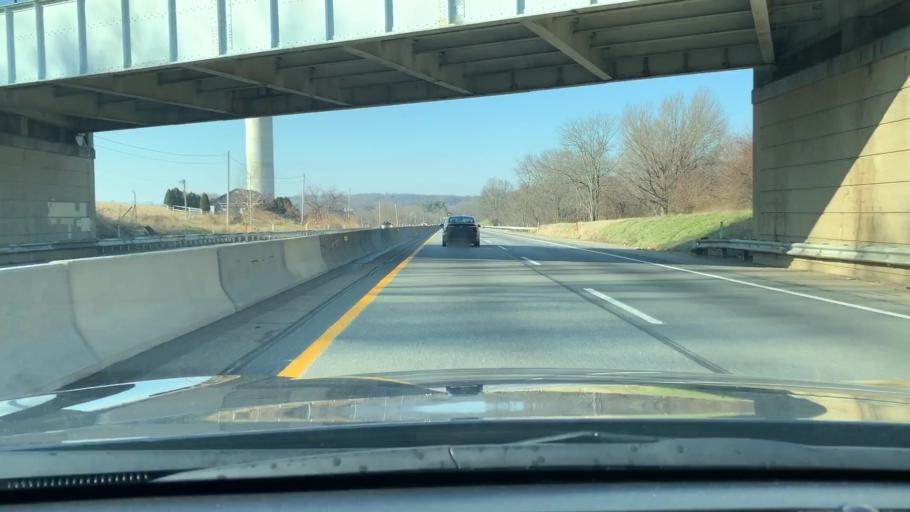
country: US
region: Pennsylvania
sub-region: Chester County
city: Downingtown
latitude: 40.0843
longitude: -75.7147
